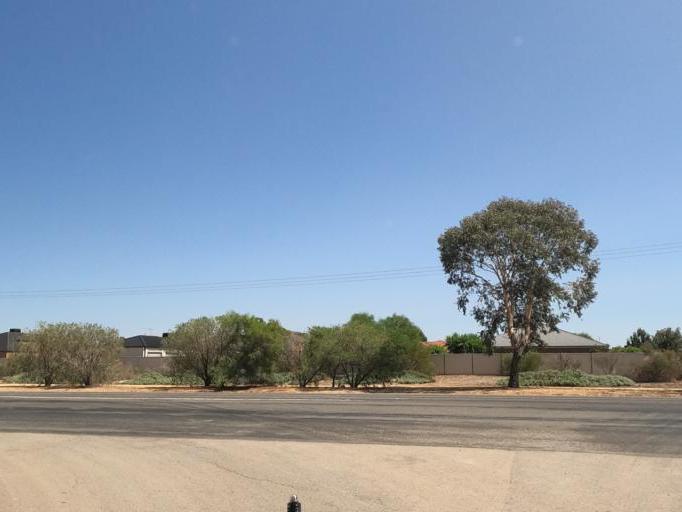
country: AU
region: Victoria
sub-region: Moira
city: Yarrawonga
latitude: -36.0116
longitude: 146.0248
